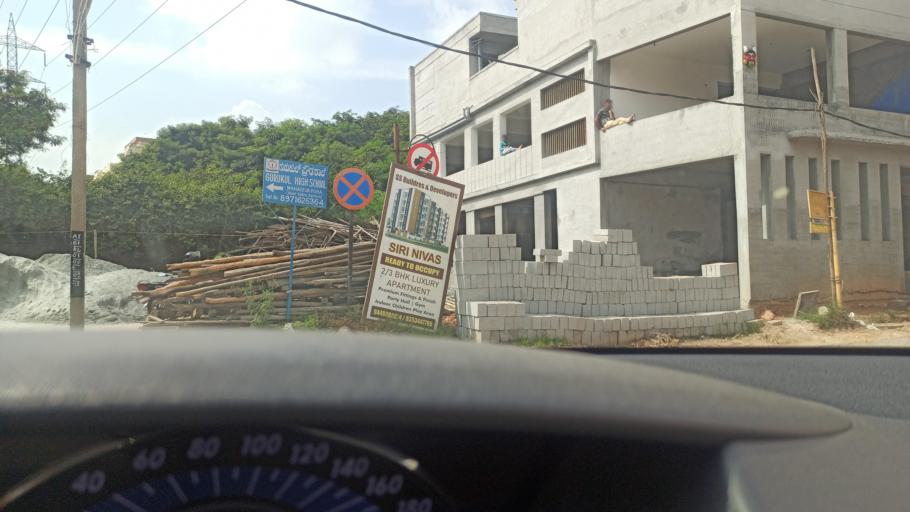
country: IN
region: Karnataka
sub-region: Bangalore Urban
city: Bangalore
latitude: 12.9874
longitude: 77.6849
